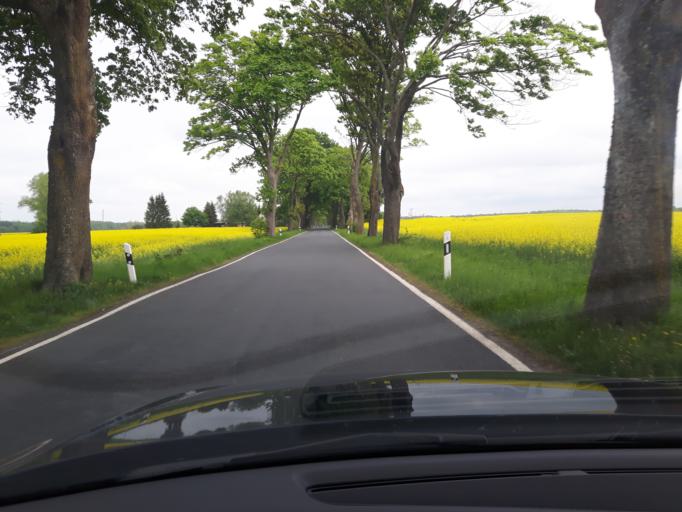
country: DE
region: Mecklenburg-Vorpommern
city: Velgast
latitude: 54.2099
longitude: 12.7326
